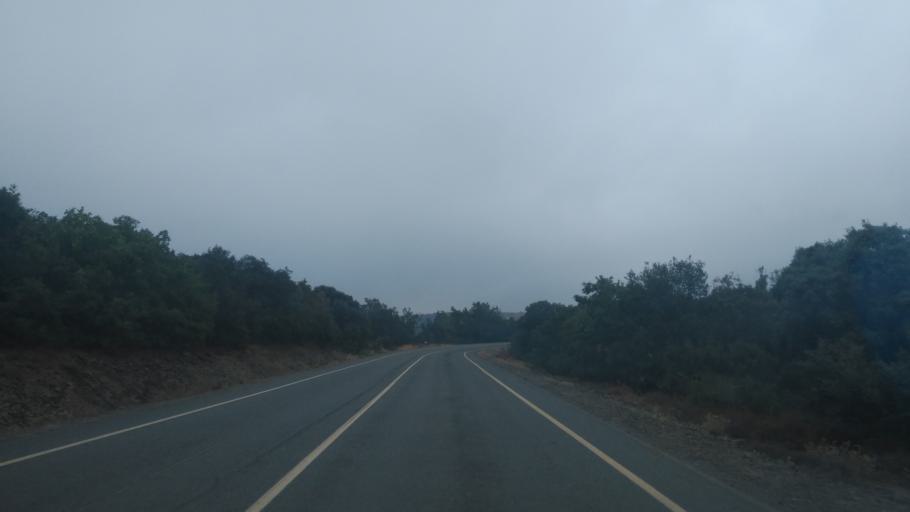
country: ES
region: Castille and Leon
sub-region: Provincia de Salamanca
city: Aldeanueva de la Sierra
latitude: 40.6040
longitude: -6.0927
